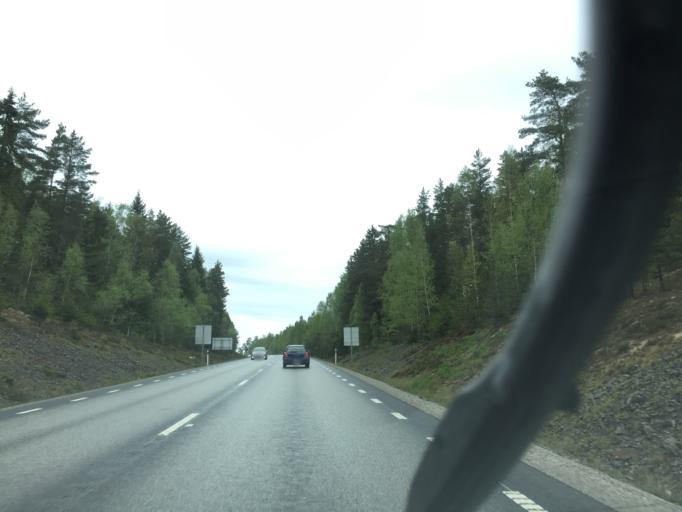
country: SE
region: OErebro
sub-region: Lindesbergs Kommun
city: Lindesberg
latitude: 59.5569
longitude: 15.2208
